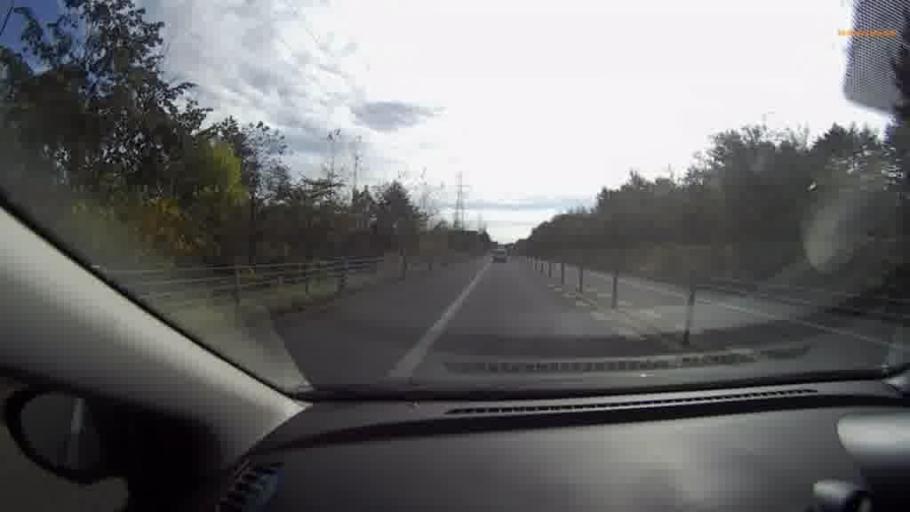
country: JP
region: Hokkaido
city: Kushiro
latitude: 43.0264
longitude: 144.4092
